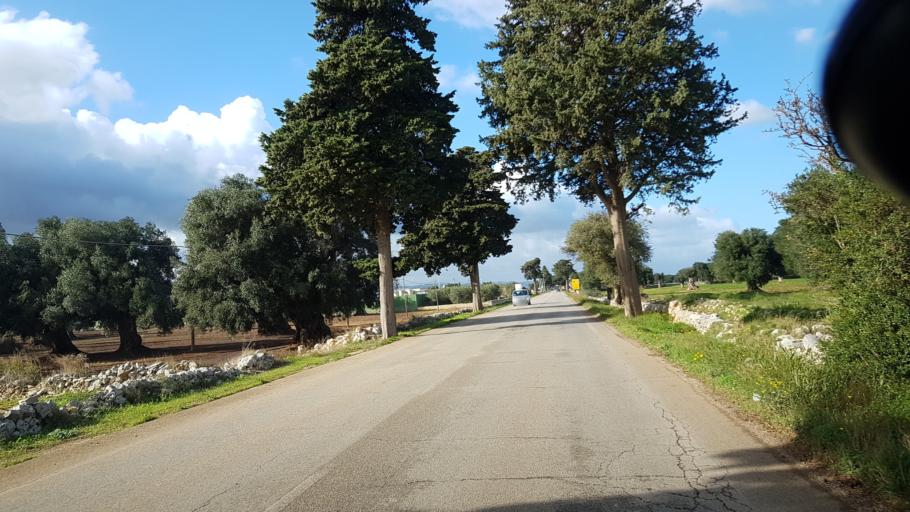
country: IT
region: Apulia
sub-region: Provincia di Brindisi
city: Montalbano
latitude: 40.7852
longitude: 17.4742
